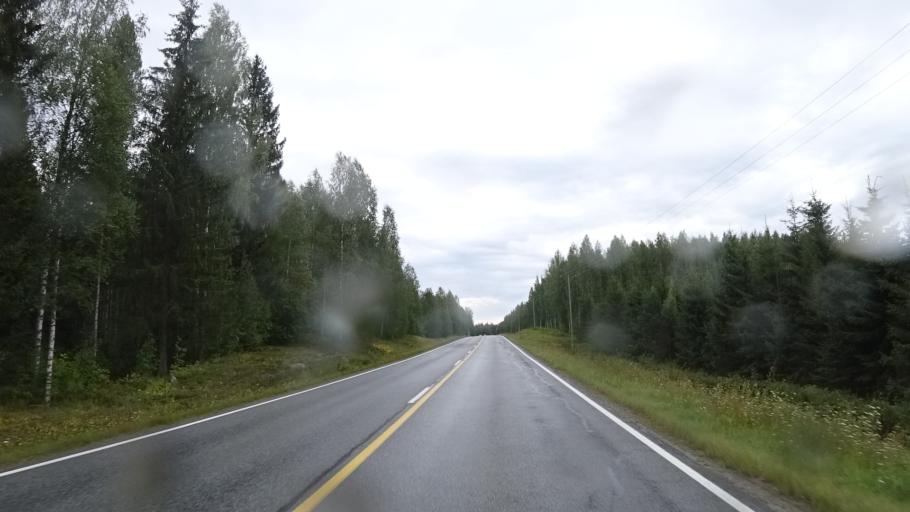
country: FI
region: North Karelia
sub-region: Keski-Karjala
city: Kesaelahti
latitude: 62.0993
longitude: 29.8500
